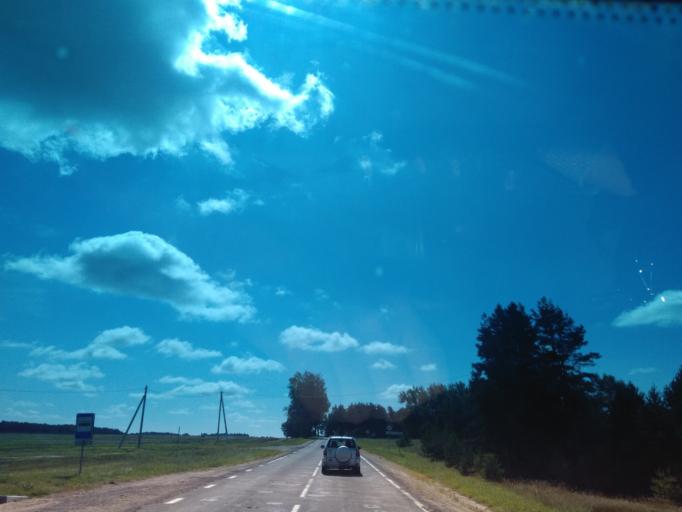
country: BY
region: Minsk
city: Uzda
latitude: 53.2913
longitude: 27.2396
